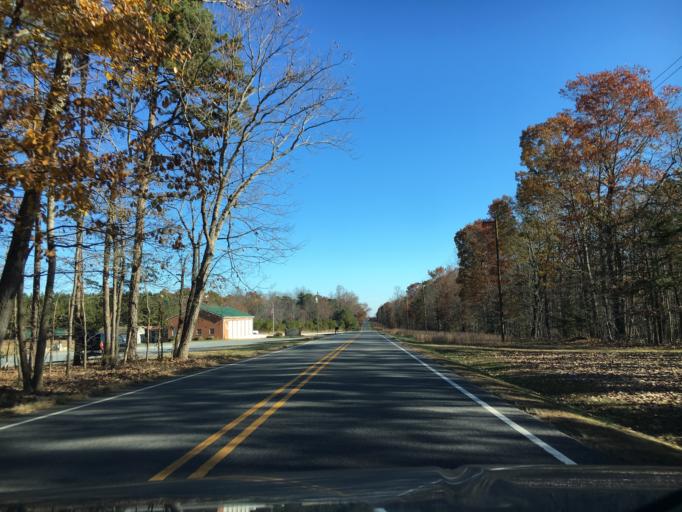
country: US
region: Virginia
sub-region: Buckingham County
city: Buckingham
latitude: 37.4605
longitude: -78.6756
